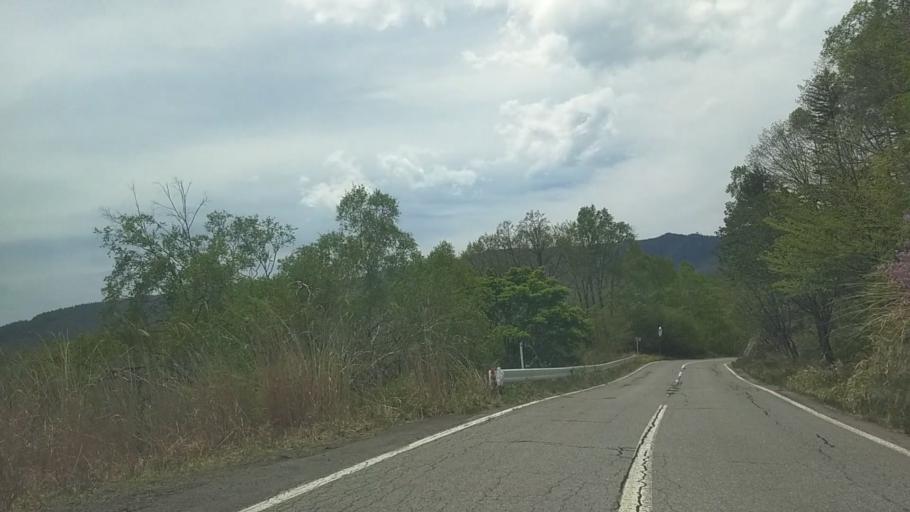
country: JP
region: Nagano
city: Saku
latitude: 36.0846
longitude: 138.3866
